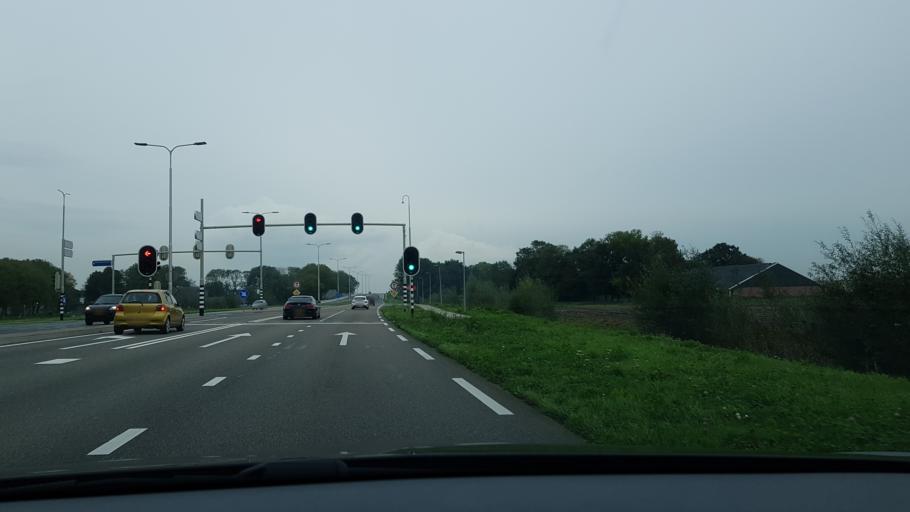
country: NL
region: South Holland
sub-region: Gemeente Kaag en Braassem
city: Leimuiden
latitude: 52.1865
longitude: 4.6739
